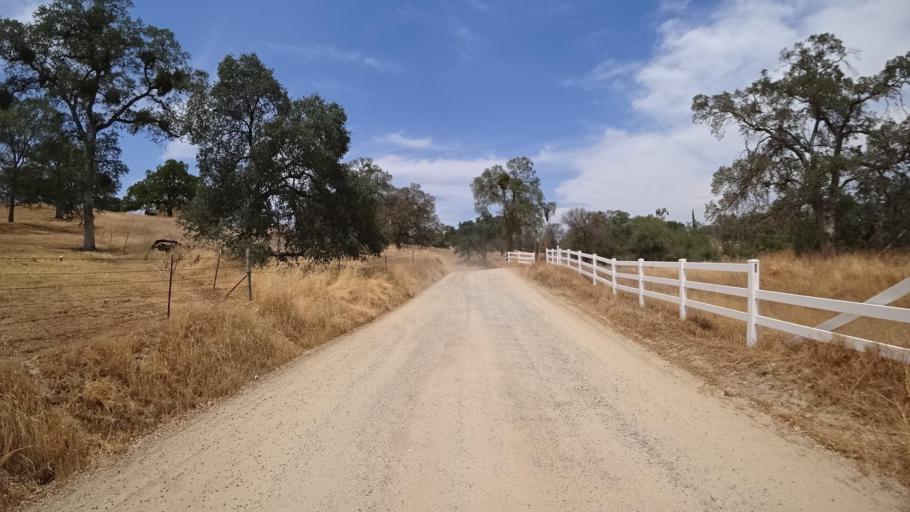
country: US
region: California
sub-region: Madera County
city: Ahwahnee
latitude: 37.3707
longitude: -119.8730
